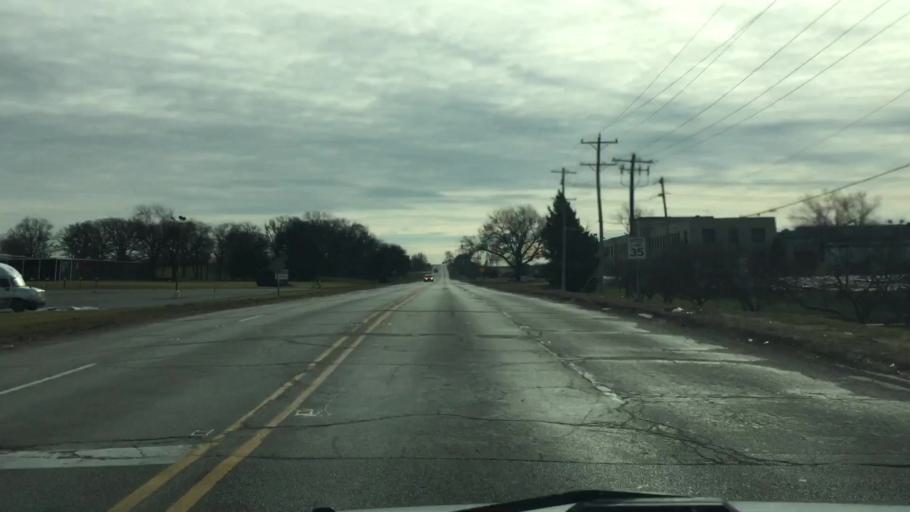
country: US
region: Illinois
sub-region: Kane County
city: Elgin
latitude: 42.0122
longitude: -88.2693
